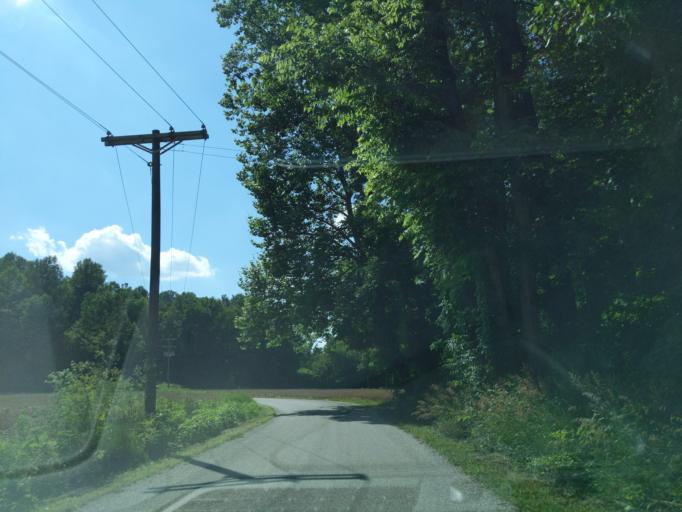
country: US
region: Indiana
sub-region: Ripley County
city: Osgood
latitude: 39.1901
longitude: -85.4091
